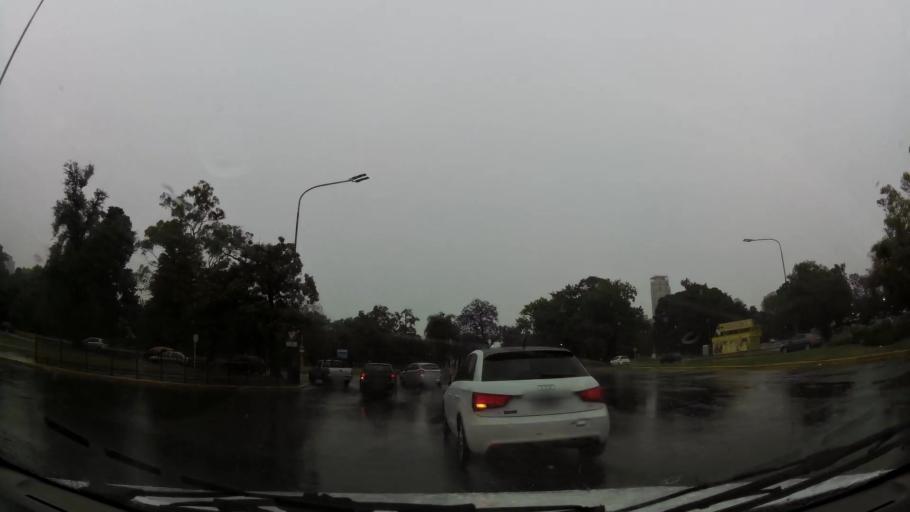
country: AR
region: Buenos Aires F.D.
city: Retiro
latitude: -34.5719
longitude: -58.4119
